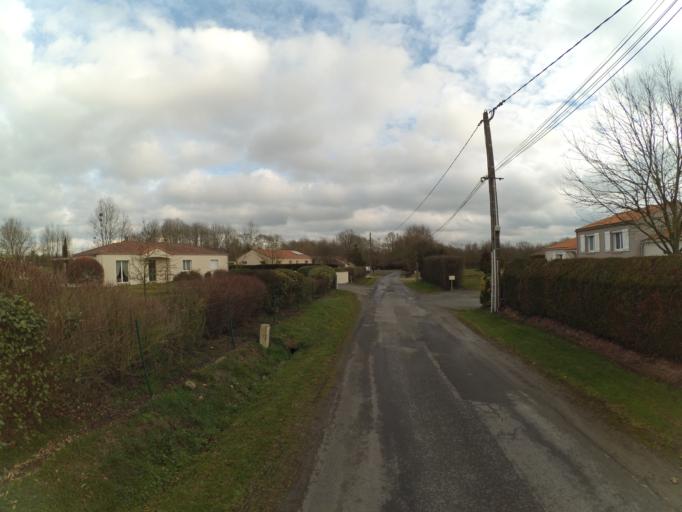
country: FR
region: Pays de la Loire
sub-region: Departement de la Vendee
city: La Bernardiere
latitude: 47.0475
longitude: -1.2861
